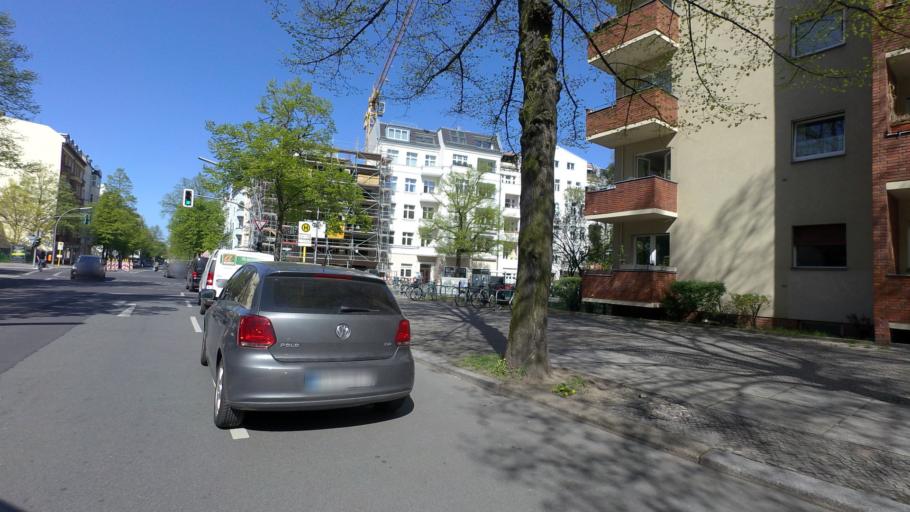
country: DE
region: Berlin
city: Halensee
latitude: 52.4955
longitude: 13.2960
